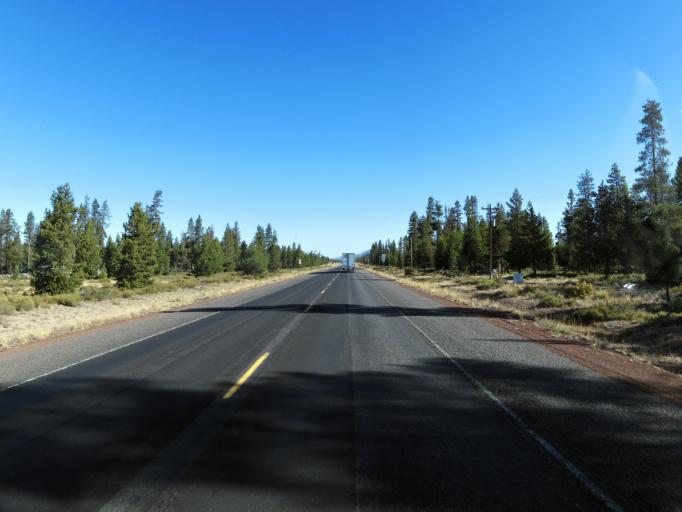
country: US
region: Oregon
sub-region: Deschutes County
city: La Pine
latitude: 43.1356
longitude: -121.8024
